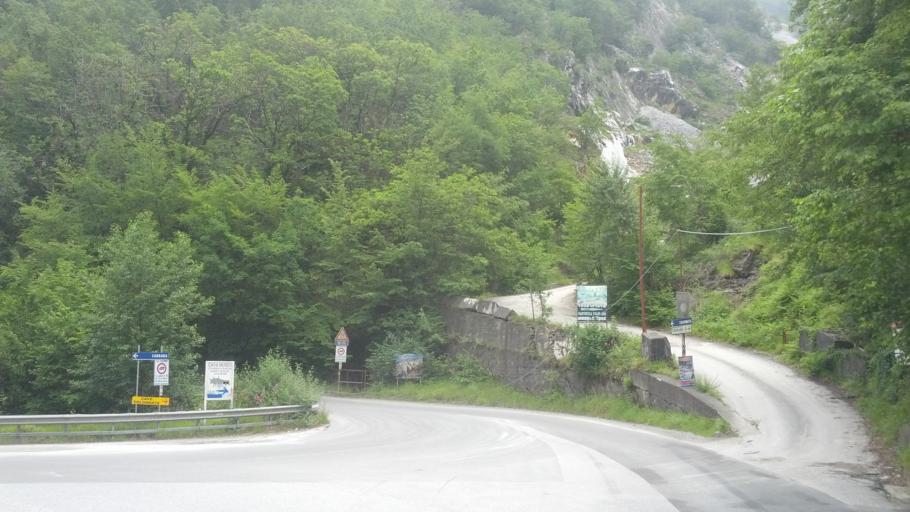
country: IT
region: Tuscany
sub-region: Provincia di Massa-Carrara
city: Massa
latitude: 44.0793
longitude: 10.1415
